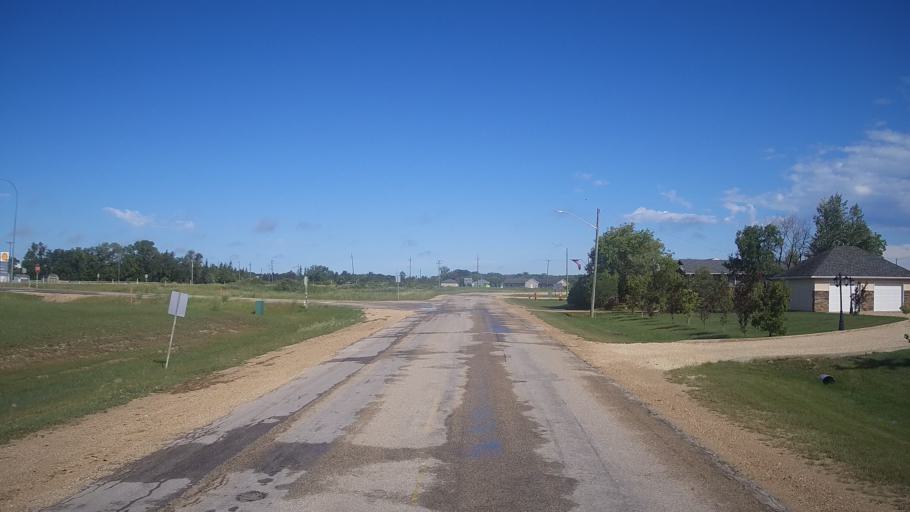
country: CA
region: Manitoba
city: Stonewall
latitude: 50.2093
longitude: -97.6642
